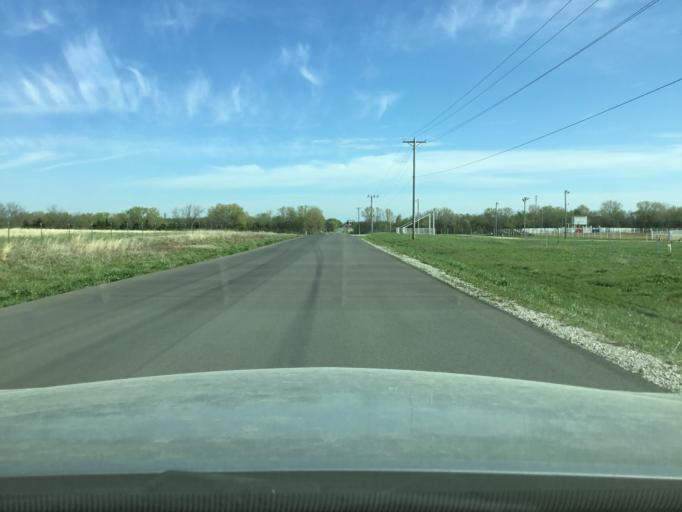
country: US
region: Kansas
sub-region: Neosho County
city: Chanute
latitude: 37.6535
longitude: -95.4435
